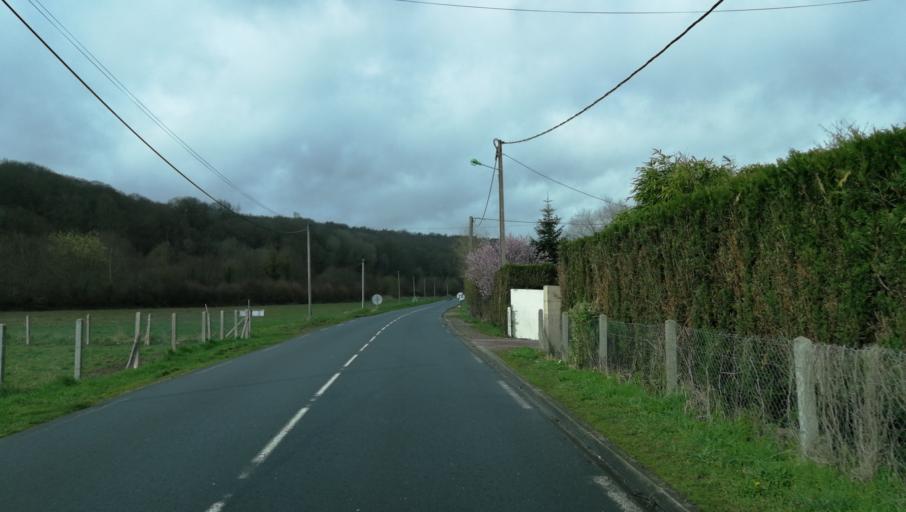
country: FR
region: Haute-Normandie
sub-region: Departement de l'Eure
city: Brionne
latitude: 49.2151
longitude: 0.7025
